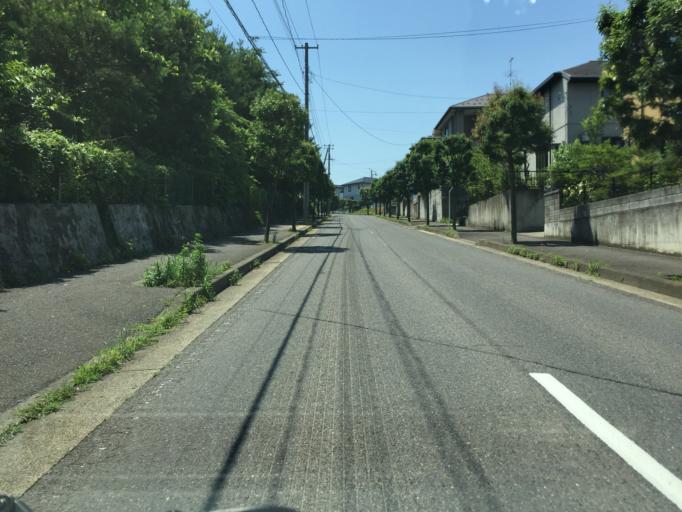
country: JP
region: Fukushima
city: Fukushima-shi
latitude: 37.7247
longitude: 140.4063
